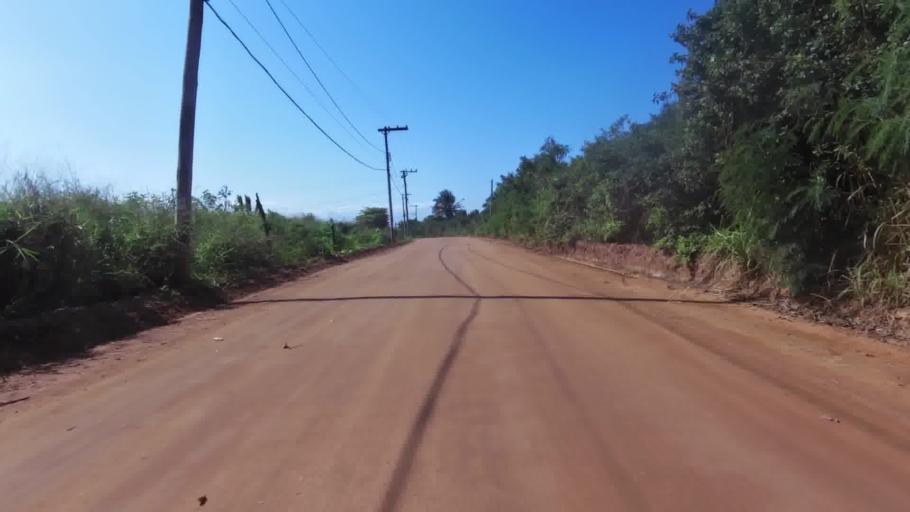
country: BR
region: Espirito Santo
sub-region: Piuma
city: Piuma
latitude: -20.8320
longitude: -40.6208
